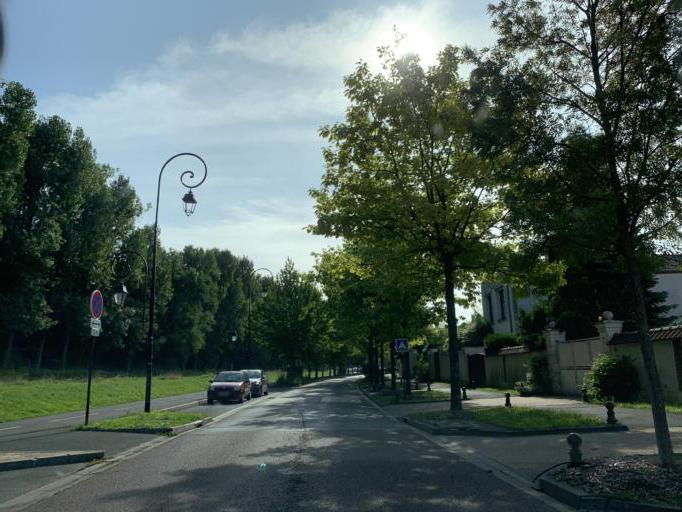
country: FR
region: Ile-de-France
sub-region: Departement de Seine-et-Marne
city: Claye-Souilly
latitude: 48.9450
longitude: 2.6935
